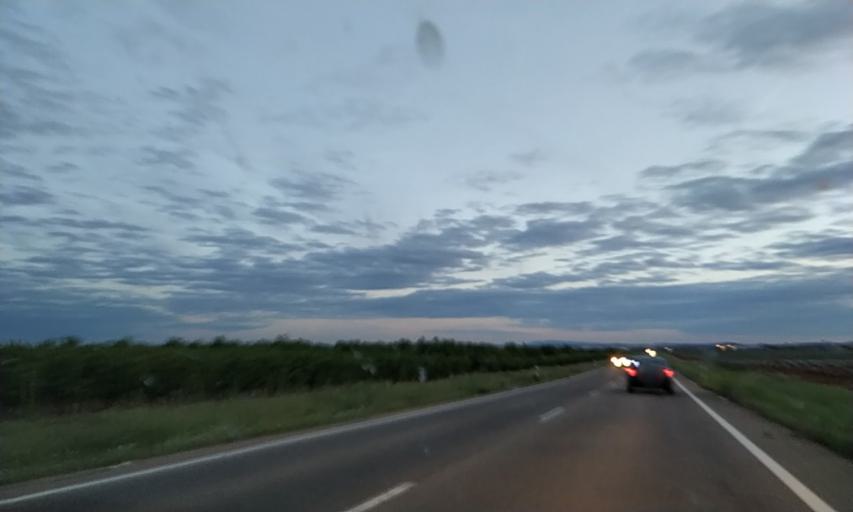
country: ES
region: Extremadura
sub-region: Provincia de Badajoz
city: Badajoz
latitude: 38.9409
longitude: -6.9201
